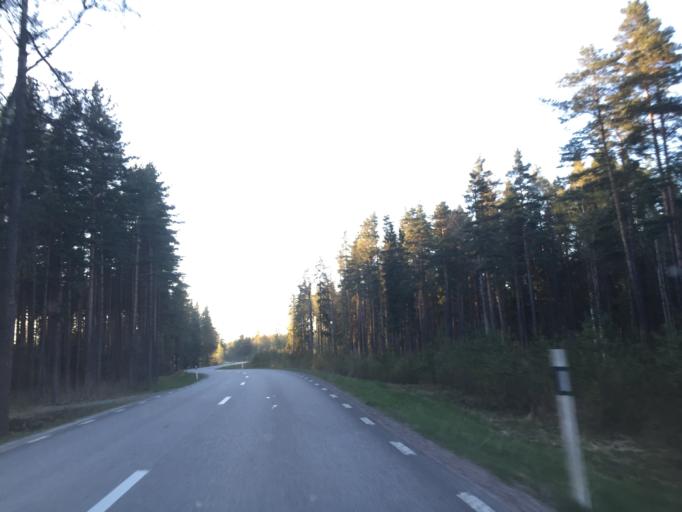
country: SE
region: OErebro
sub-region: Hallsbergs Kommun
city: Skollersta
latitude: 59.2426
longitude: 15.4016
